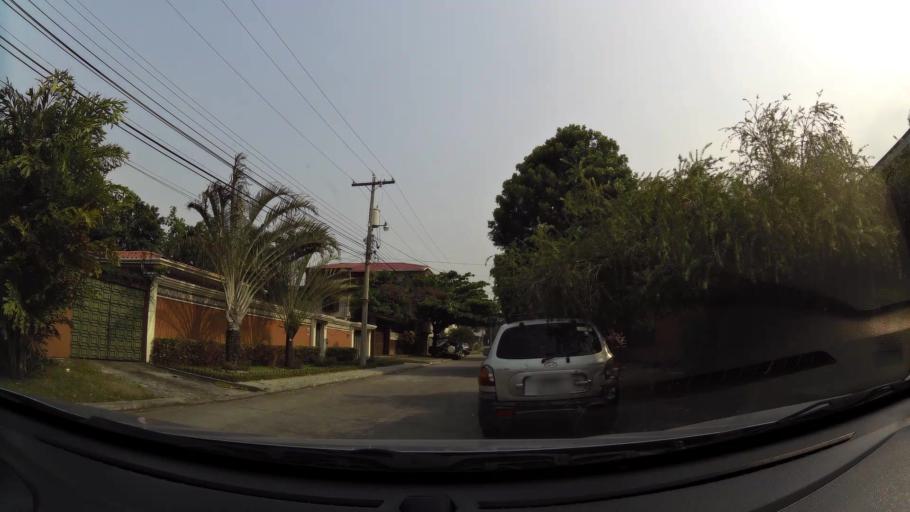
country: HN
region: Cortes
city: El Zapotal del Norte
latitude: 15.5099
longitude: -88.0398
